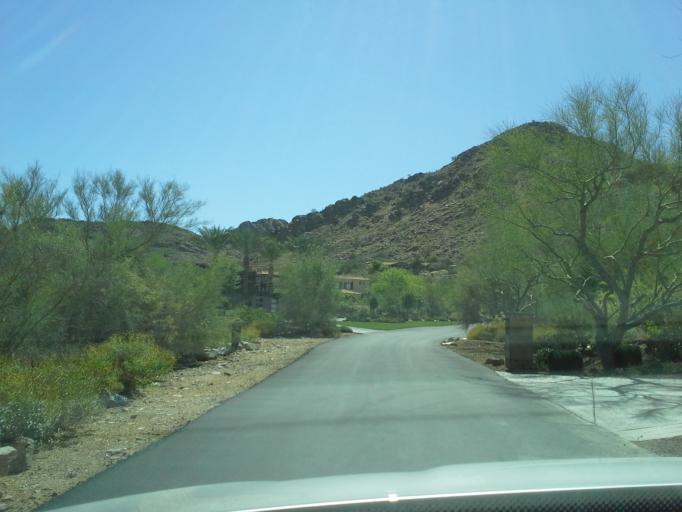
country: US
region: Arizona
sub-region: Maricopa County
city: Paradise Valley
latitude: 33.5512
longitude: -111.9491
